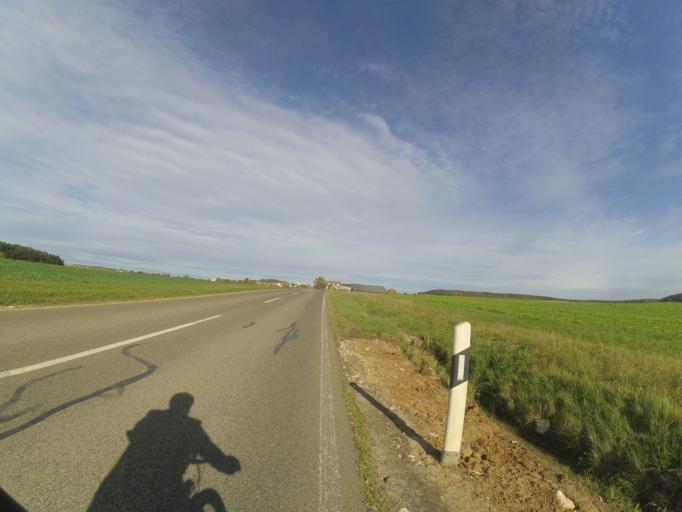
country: DE
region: Baden-Wuerttemberg
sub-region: Tuebingen Region
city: Lonsee
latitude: 48.5741
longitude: 9.9187
